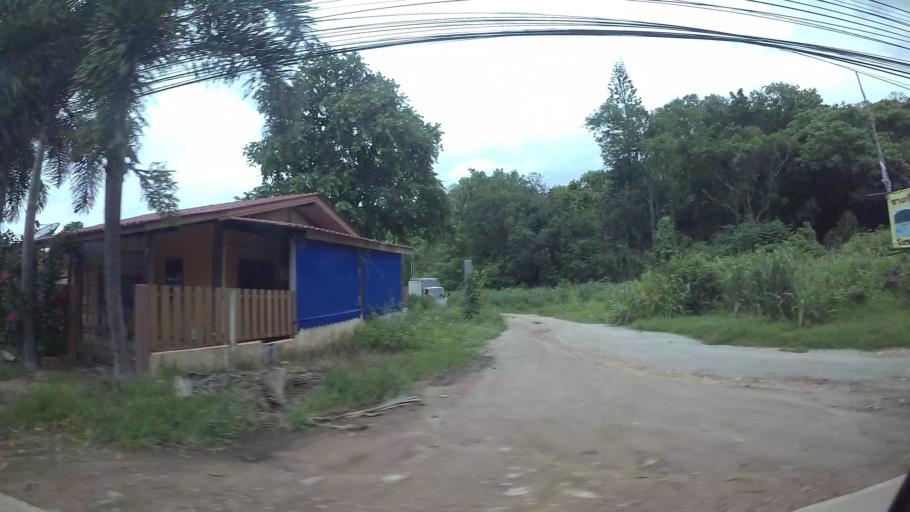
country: TH
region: Chon Buri
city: Si Racha
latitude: 13.2002
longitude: 100.9554
